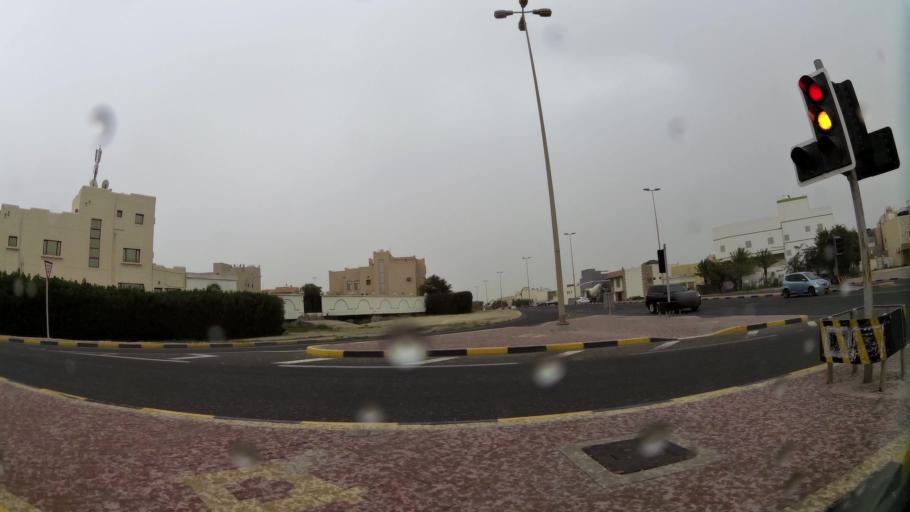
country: BH
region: Northern
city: Madinat `Isa
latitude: 26.1557
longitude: 50.5740
